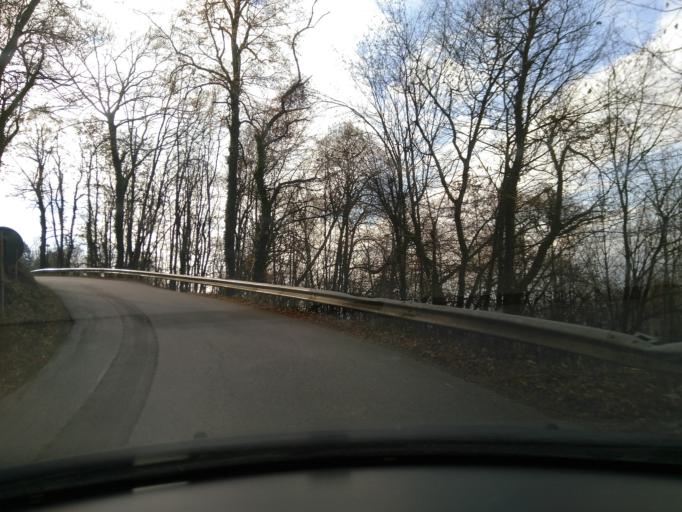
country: FR
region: Rhone-Alpes
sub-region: Departement de l'Isere
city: Villard-Bonnot
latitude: 45.2501
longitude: 5.9052
